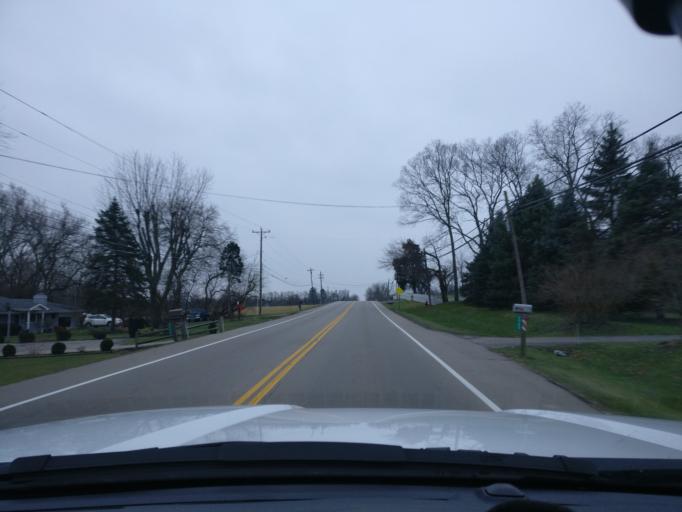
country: US
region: Ohio
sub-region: Warren County
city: Lebanon
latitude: 39.4744
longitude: -84.2023
